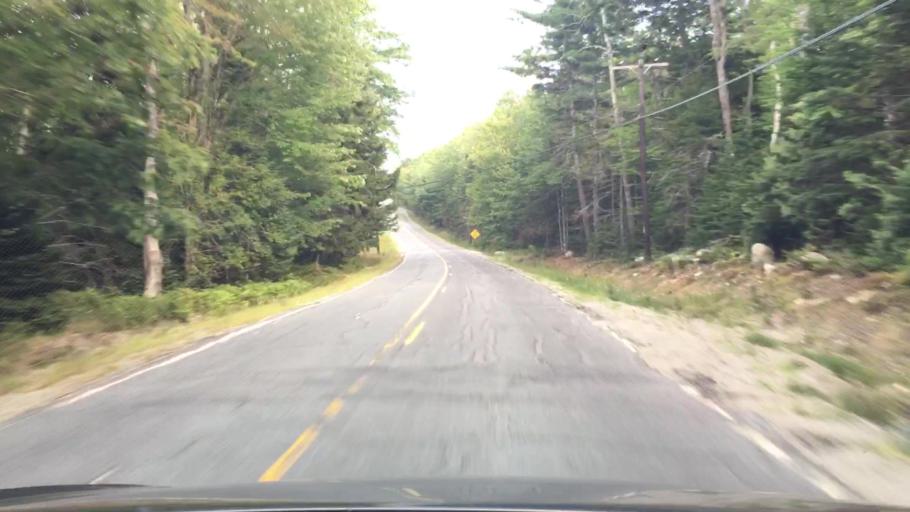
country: US
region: Maine
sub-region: Hancock County
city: Surry
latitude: 44.5005
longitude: -68.5711
